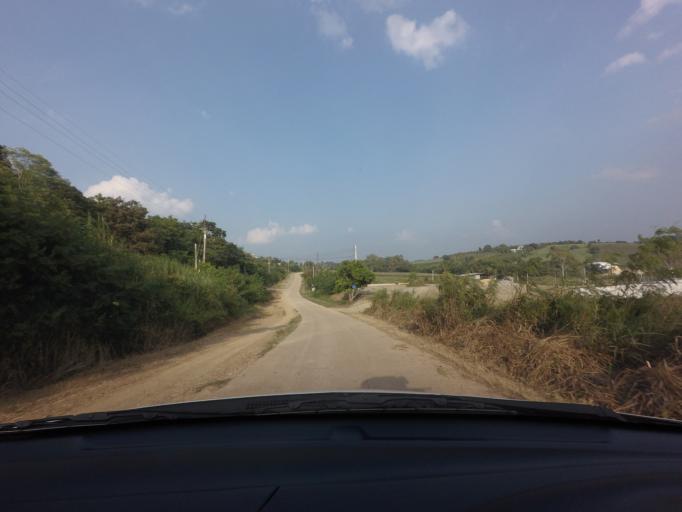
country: TH
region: Nakhon Ratchasima
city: Pak Chong
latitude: 14.5304
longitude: 101.5796
